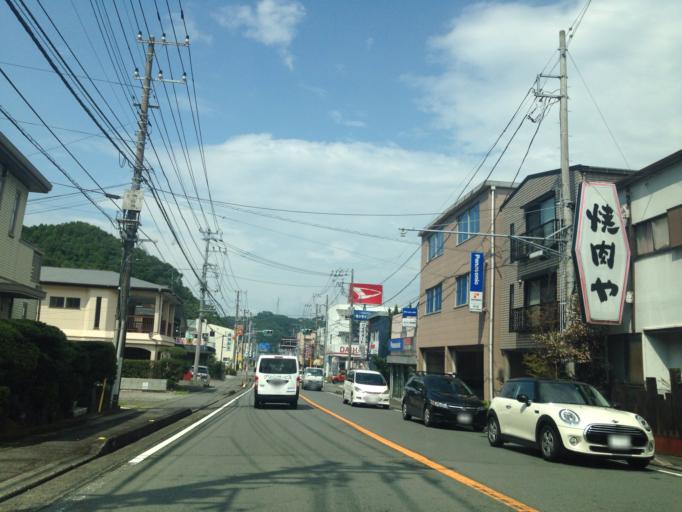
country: JP
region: Shizuoka
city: Ito
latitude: 34.9815
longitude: 138.9484
